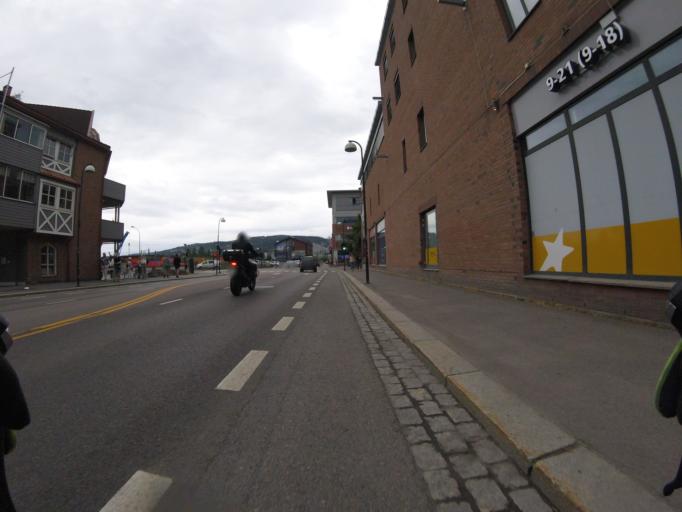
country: NO
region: Akershus
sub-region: Skedsmo
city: Lillestrom
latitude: 59.9566
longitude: 11.0507
